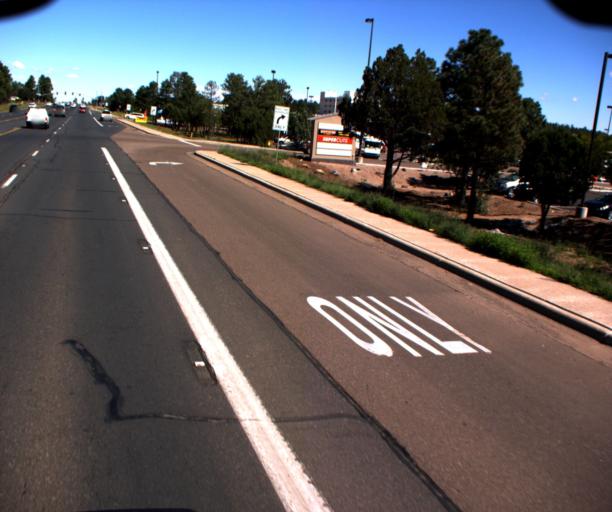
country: US
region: Arizona
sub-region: Navajo County
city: Lake of the Woods
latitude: 34.1988
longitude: -110.0177
